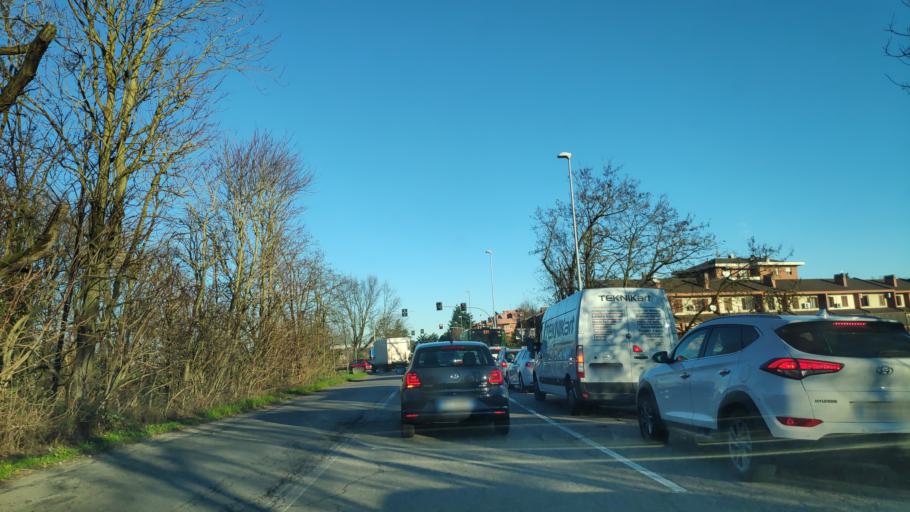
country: IT
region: Lombardy
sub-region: Citta metropolitana di Milano
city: Fizzonasco
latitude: 45.3663
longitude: 9.1896
